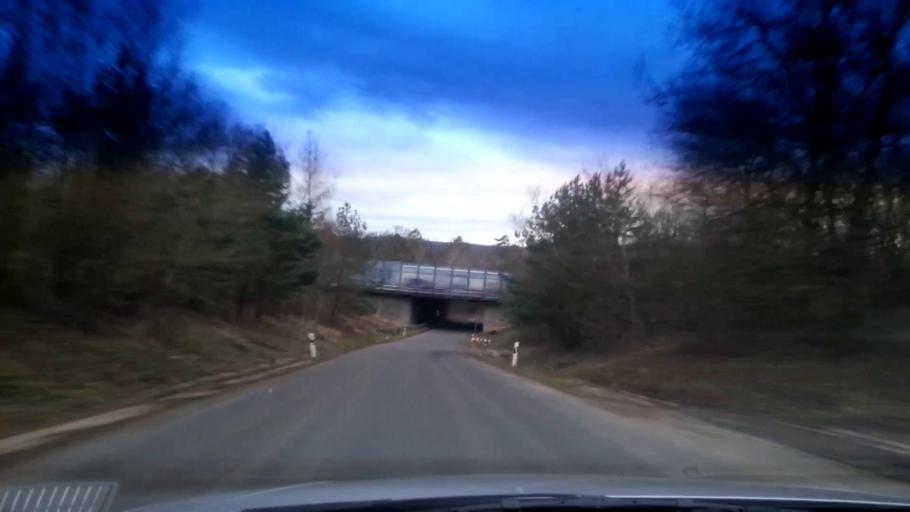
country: DE
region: Bavaria
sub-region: Upper Franconia
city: Schesslitz
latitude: 49.9833
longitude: 11.0625
